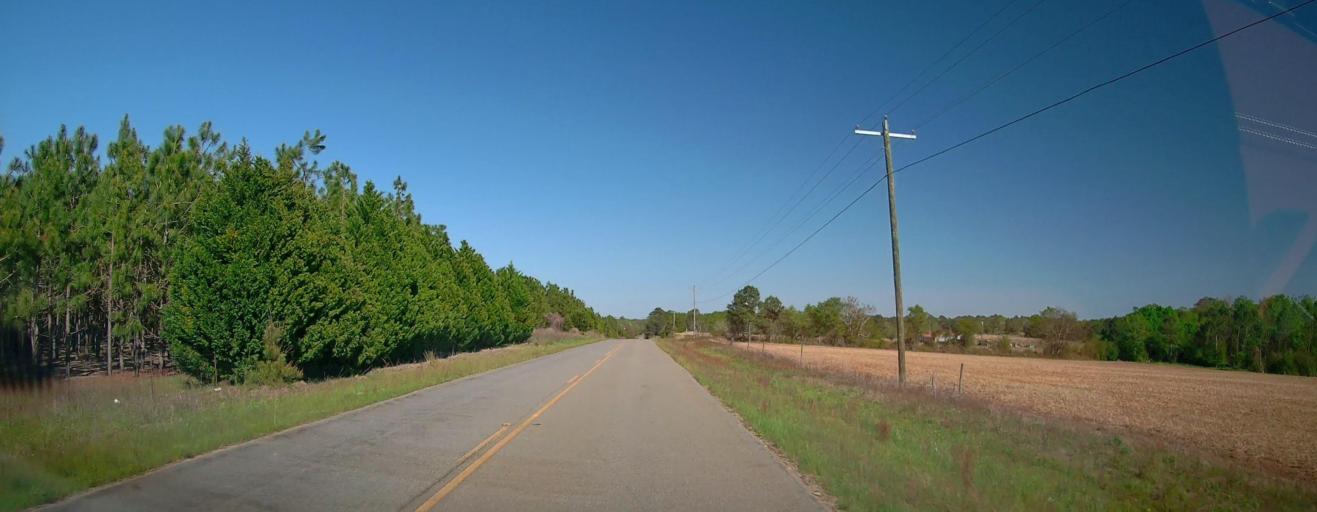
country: US
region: Georgia
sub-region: Pulaski County
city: Hawkinsville
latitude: 32.2405
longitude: -83.5239
